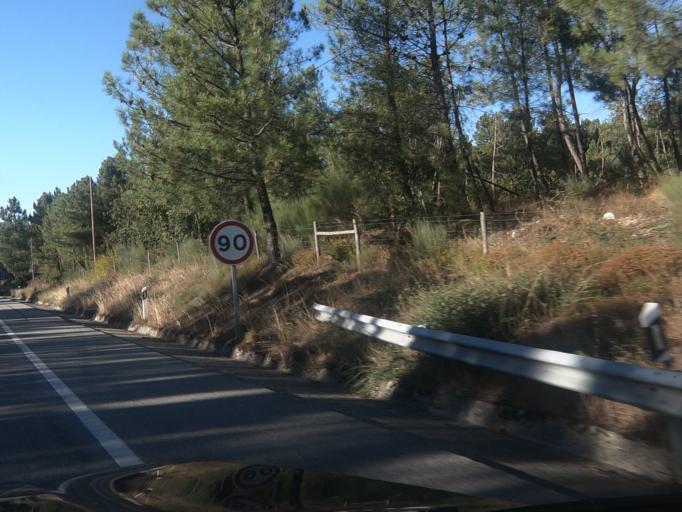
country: PT
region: Vila Real
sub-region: Vila Real
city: Vila Real
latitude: 41.3205
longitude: -7.6655
